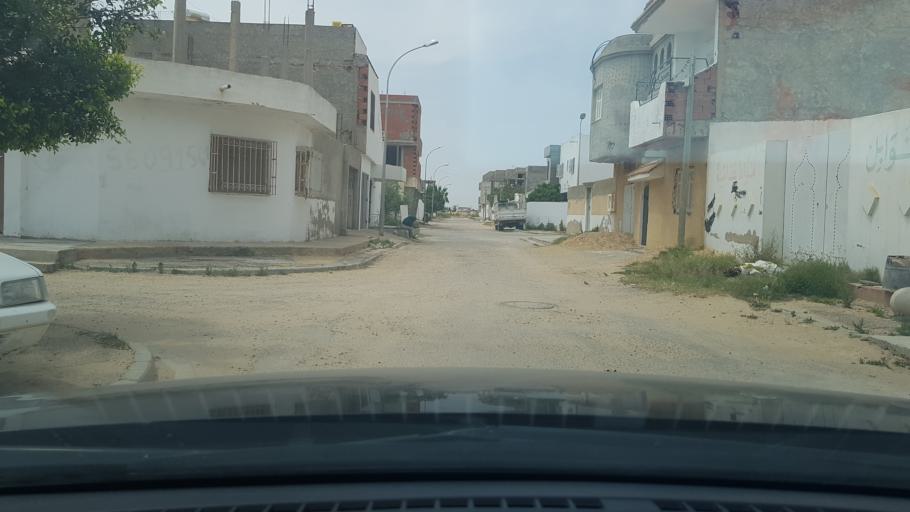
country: TN
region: Safaqis
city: Al Qarmadah
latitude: 34.8258
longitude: 10.7477
